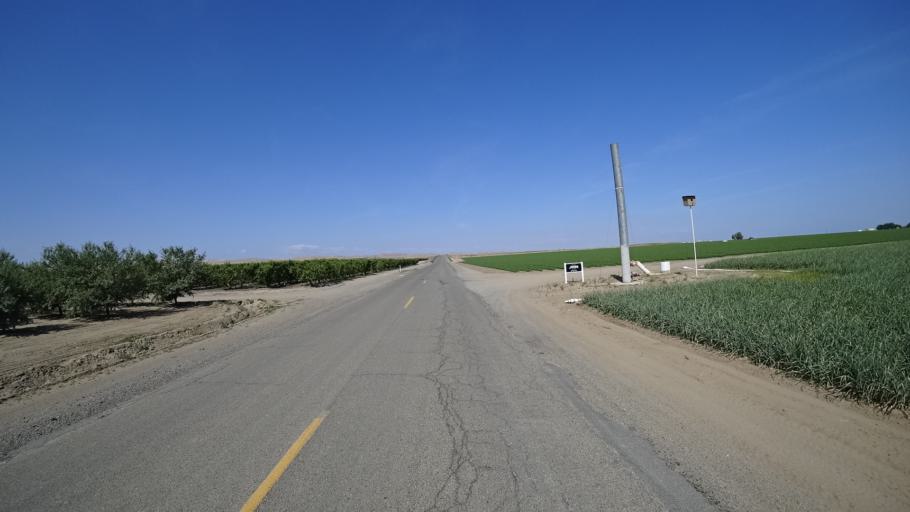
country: US
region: California
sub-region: Kings County
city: Kettleman City
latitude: 36.0363
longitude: -119.9852
